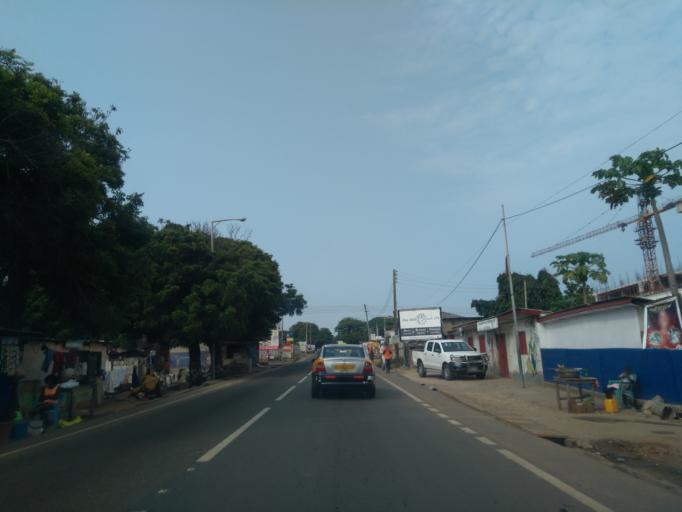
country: GH
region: Greater Accra
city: Accra
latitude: 5.5510
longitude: -0.1812
